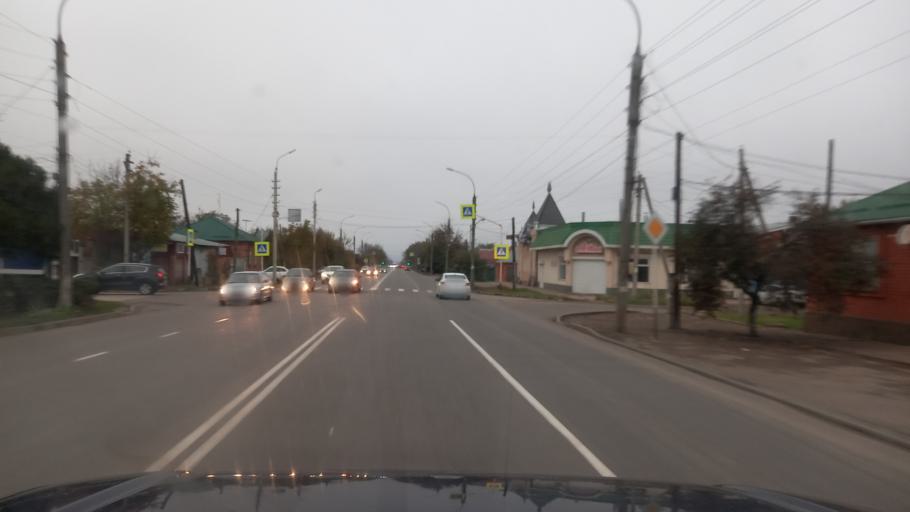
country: RU
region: Adygeya
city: Maykop
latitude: 44.6181
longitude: 40.1004
